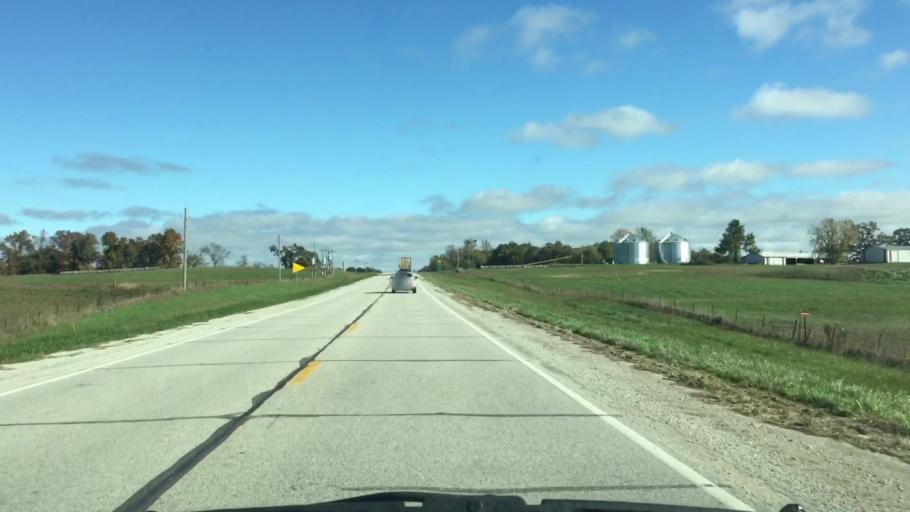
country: US
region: Iowa
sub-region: Decatur County
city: Leon
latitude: 40.6459
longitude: -93.8045
